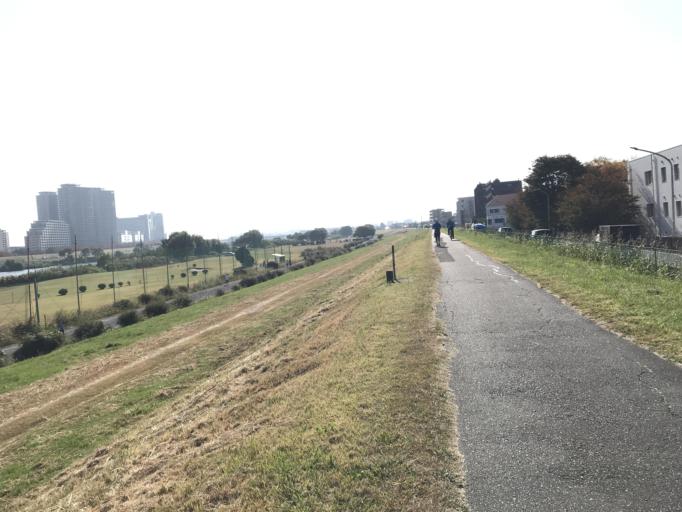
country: JP
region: Kanagawa
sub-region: Kawasaki-shi
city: Kawasaki
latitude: 35.5734
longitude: 139.6711
